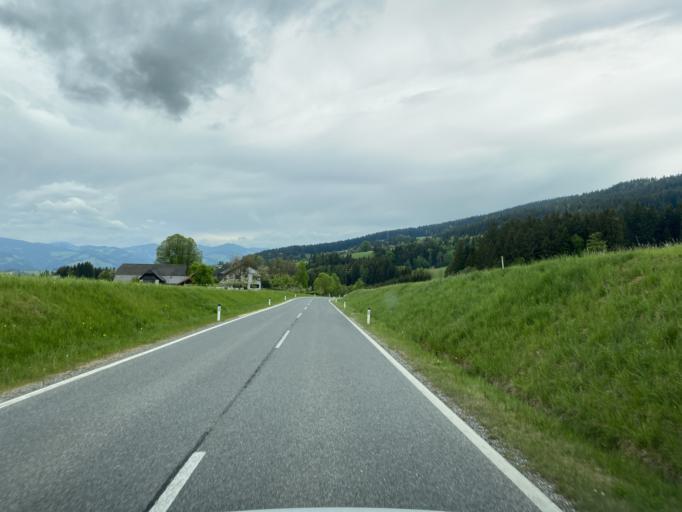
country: AT
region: Styria
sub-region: Politischer Bezirk Weiz
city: Gschaid bei Birkfeld
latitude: 47.3405
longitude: 15.7450
